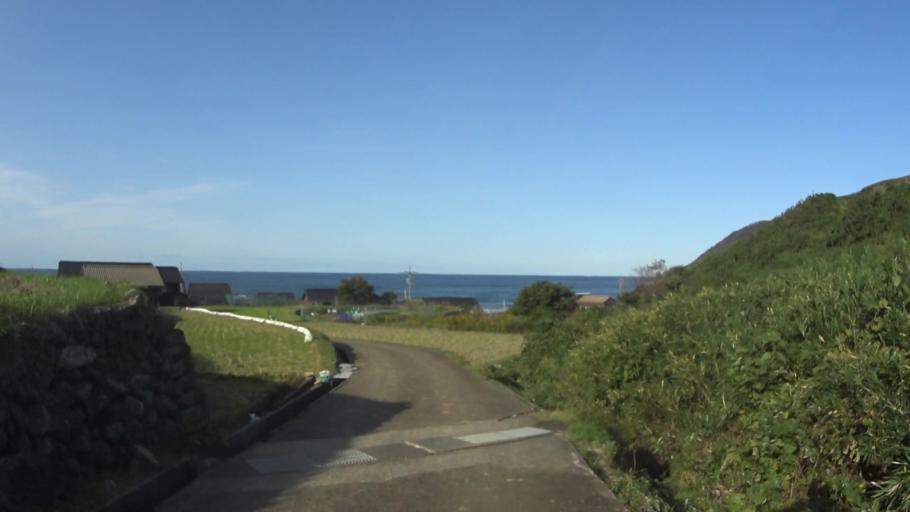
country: JP
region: Kyoto
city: Miyazu
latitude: 35.7621
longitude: 135.2065
